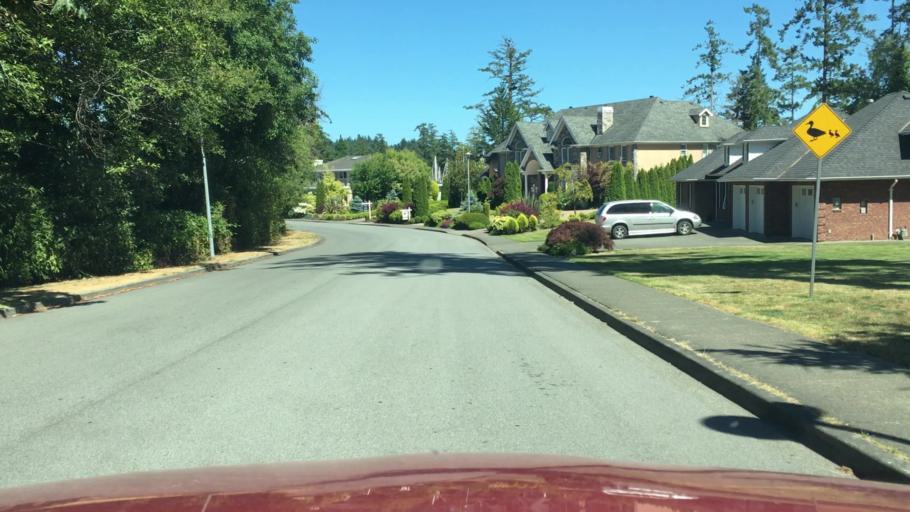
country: CA
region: British Columbia
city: North Saanich
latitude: 48.6747
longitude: -123.4233
